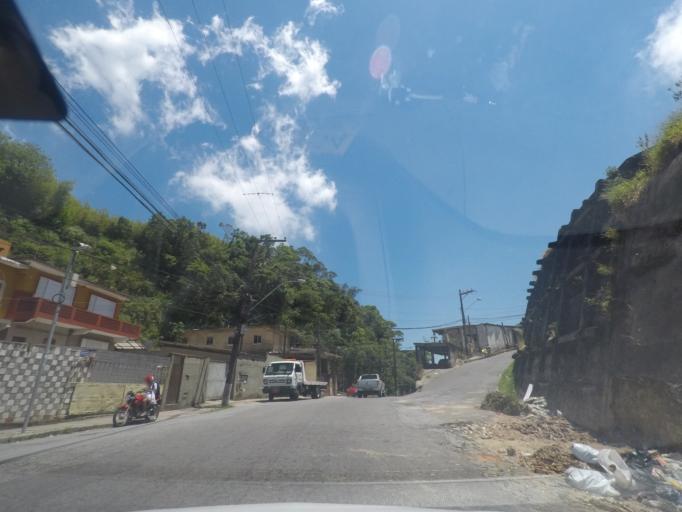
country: BR
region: Rio de Janeiro
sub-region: Petropolis
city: Petropolis
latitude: -22.5314
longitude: -43.1726
